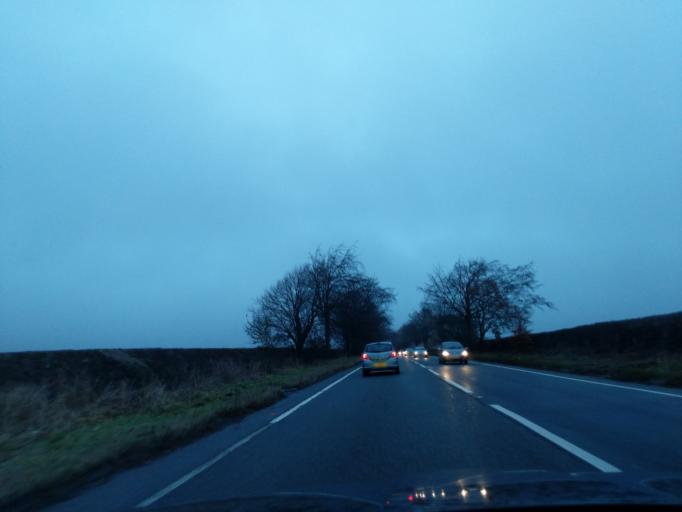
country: GB
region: England
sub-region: Northumberland
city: Hebron
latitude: 55.2077
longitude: -1.7107
